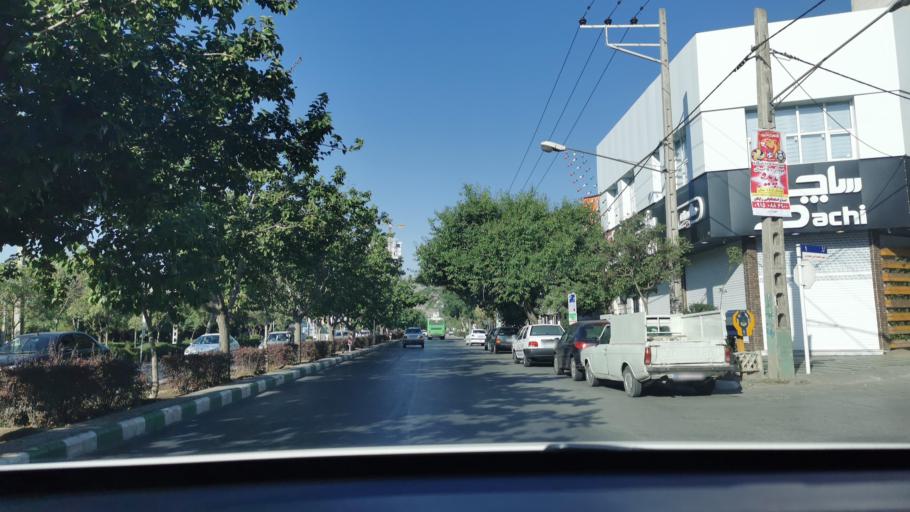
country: IR
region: Razavi Khorasan
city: Mashhad
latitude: 36.3183
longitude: 59.5230
